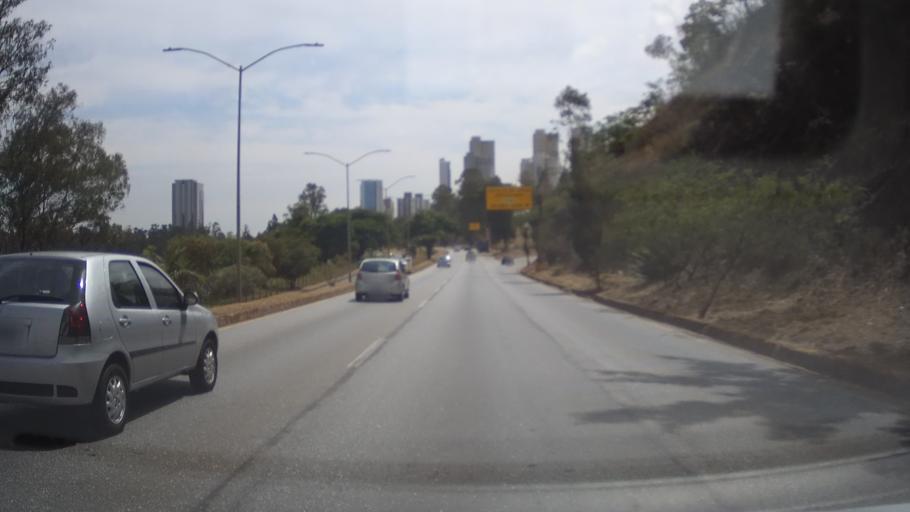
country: BR
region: Minas Gerais
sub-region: Belo Horizonte
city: Belo Horizonte
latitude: -19.9840
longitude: -43.9512
